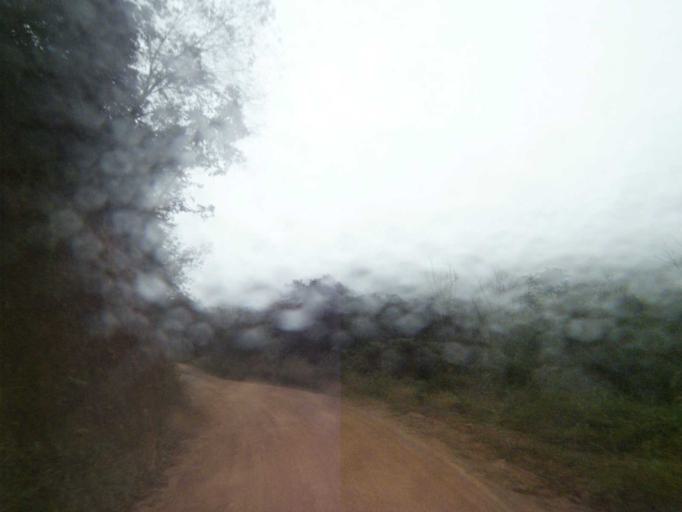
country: BR
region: Santa Catarina
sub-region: Anitapolis
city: Anitapolis
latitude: -27.8585
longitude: -49.1329
